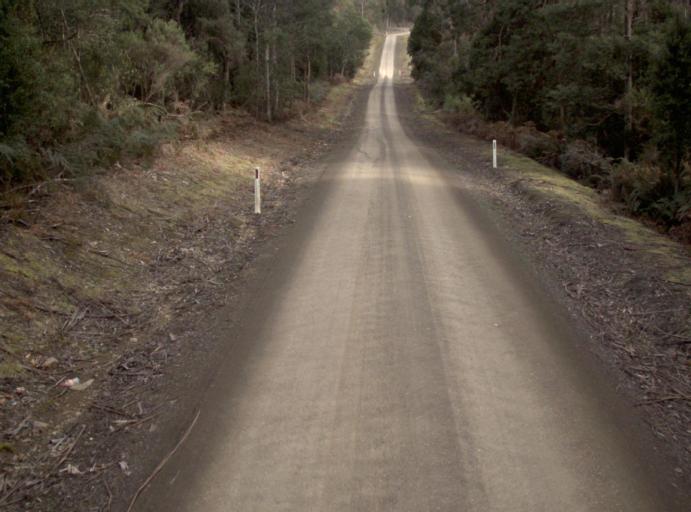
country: AU
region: Tasmania
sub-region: Dorset
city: Scottsdale
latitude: -41.2762
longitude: 147.3426
